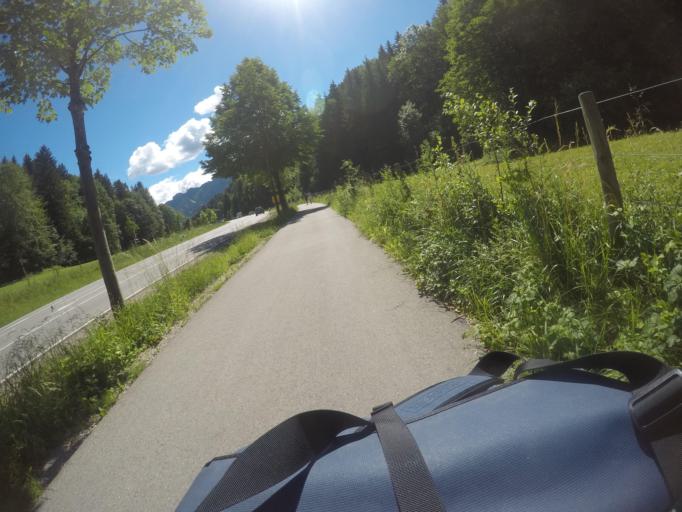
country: DE
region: Bavaria
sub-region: Swabia
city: Fuessen
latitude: 47.5649
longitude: 10.7119
